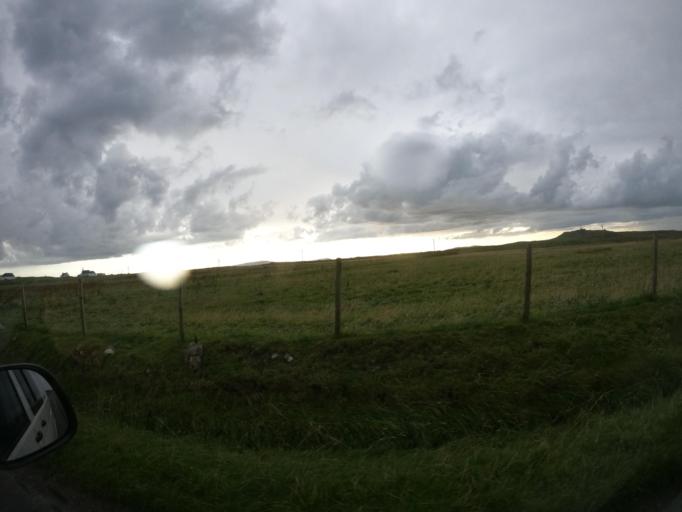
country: GB
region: Scotland
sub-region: Eilean Siar
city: Barra
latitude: 56.5049
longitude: -6.8080
